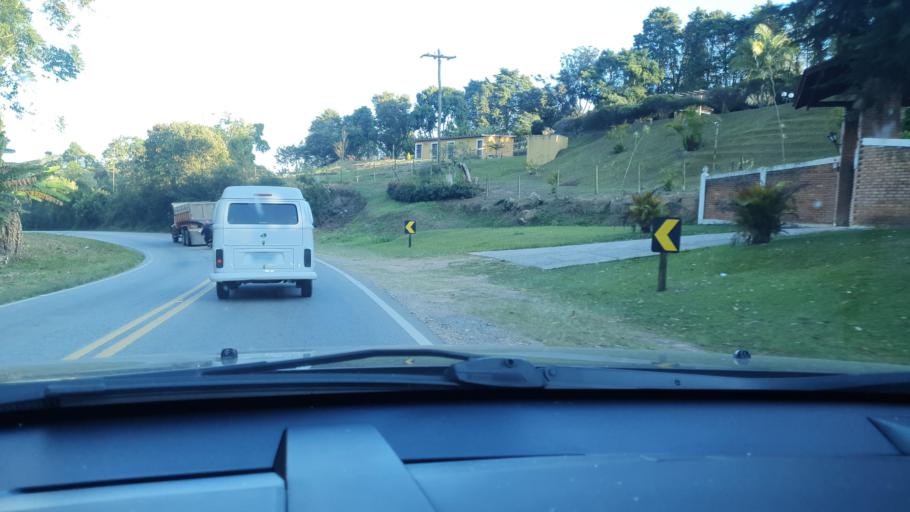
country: BR
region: Sao Paulo
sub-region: Piedade
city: Piedade
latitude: -23.7140
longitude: -47.3722
